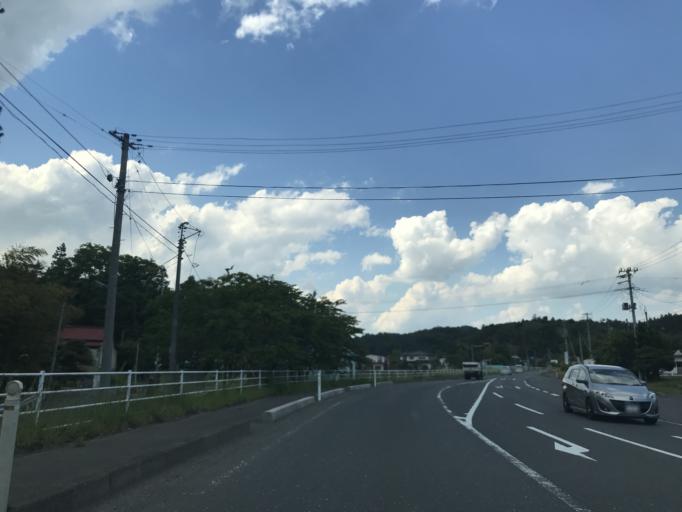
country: JP
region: Miyagi
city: Wakuya
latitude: 38.5464
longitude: 141.1410
